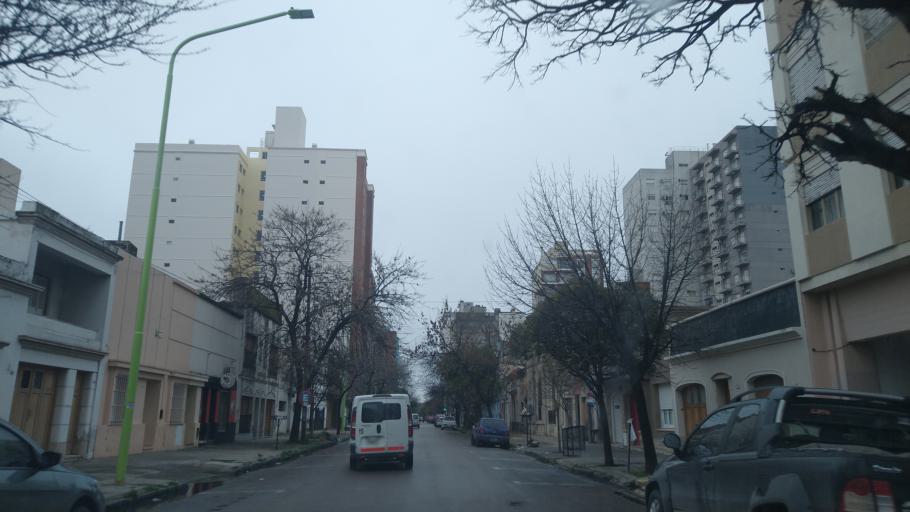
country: AR
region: Buenos Aires
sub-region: Partido de Bahia Blanca
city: Bahia Blanca
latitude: -38.7145
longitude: -62.2701
